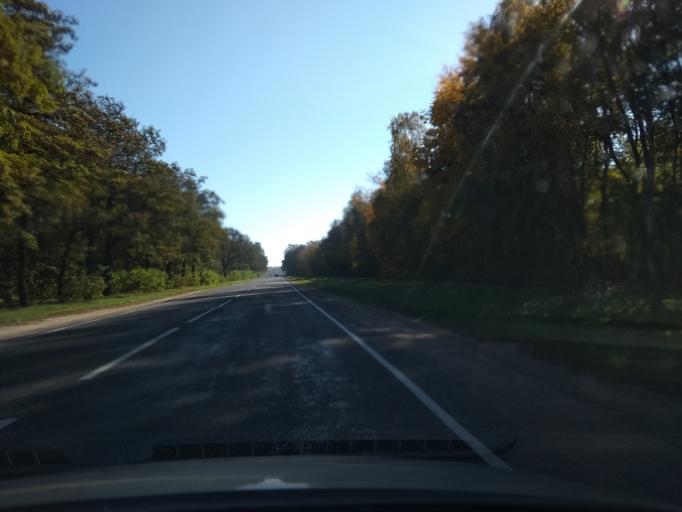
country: BY
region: Brest
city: Malaryta
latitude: 51.9314
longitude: 24.0585
